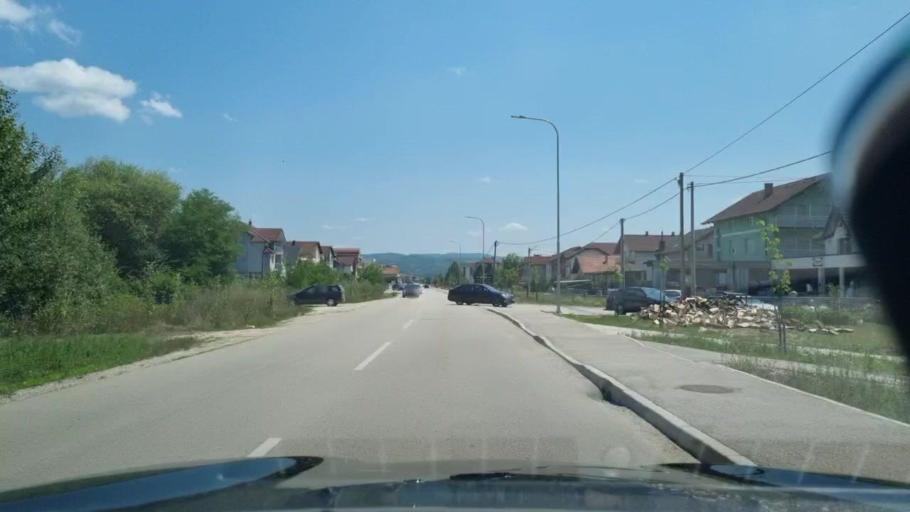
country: BA
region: Federation of Bosnia and Herzegovina
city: Sanski Most
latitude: 44.7711
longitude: 16.6493
